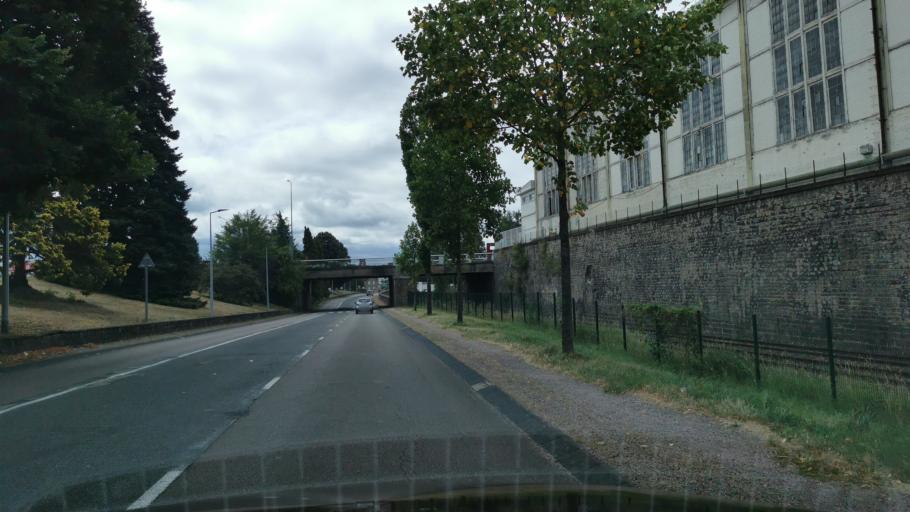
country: FR
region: Bourgogne
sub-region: Departement de Saone-et-Loire
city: Le Creusot
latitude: 46.8002
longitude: 4.4387
